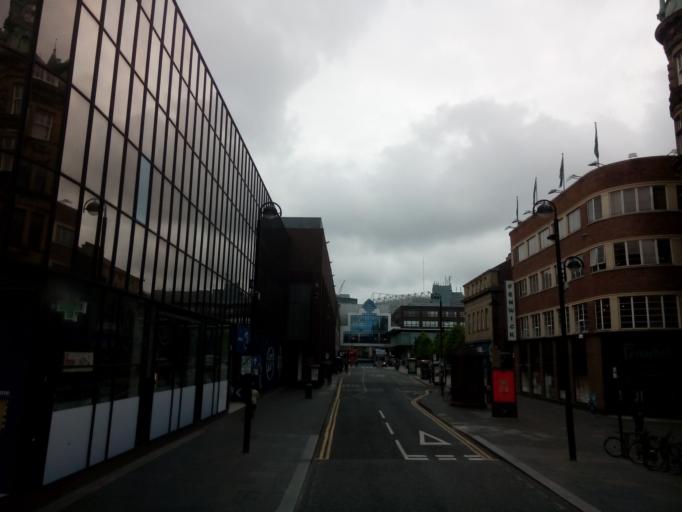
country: GB
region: England
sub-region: Newcastle upon Tyne
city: Newcastle upon Tyne
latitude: 54.9741
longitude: -1.6131
